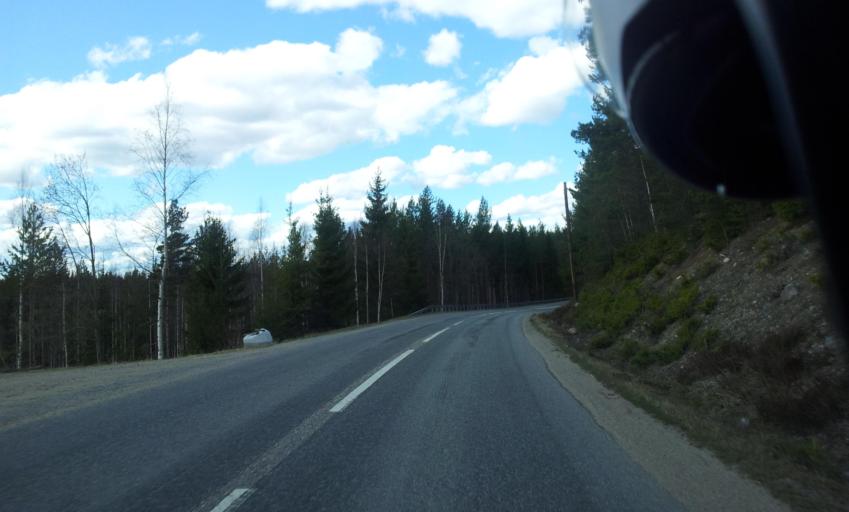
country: SE
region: Gaevleborg
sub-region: Ovanakers Kommun
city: Edsbyn
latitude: 61.2935
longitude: 15.8933
